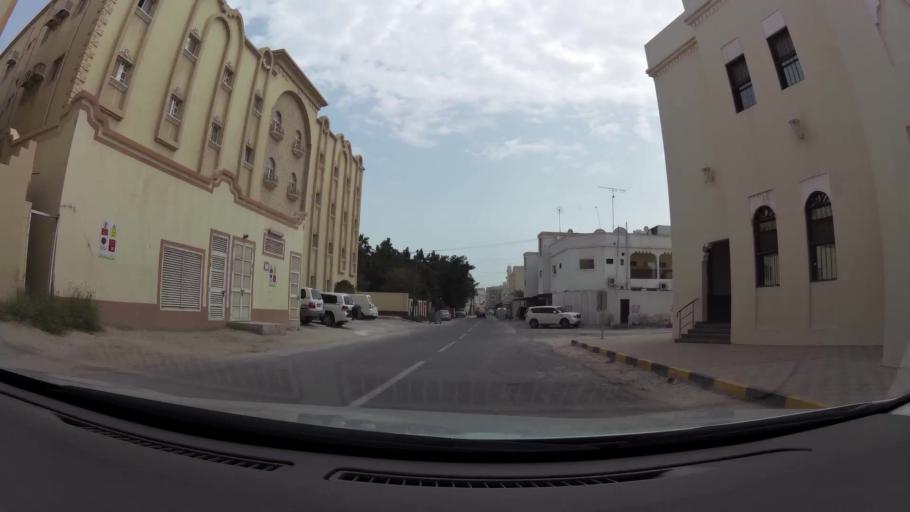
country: QA
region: Baladiyat ad Dawhah
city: Doha
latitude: 25.3075
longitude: 51.4922
